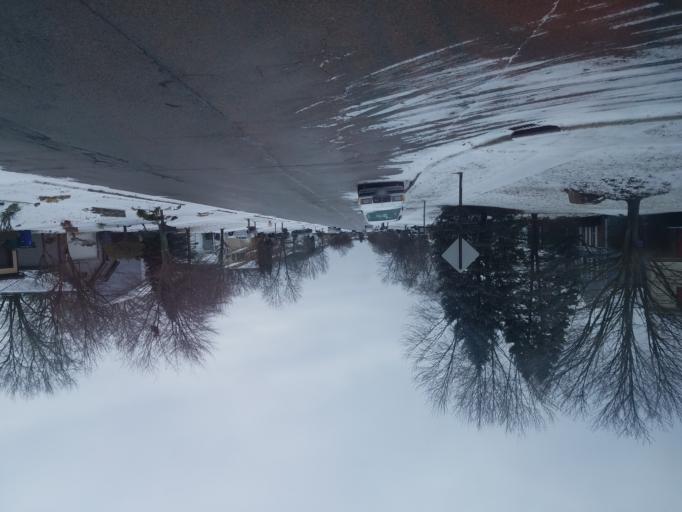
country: US
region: Ohio
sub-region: Delaware County
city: Powell
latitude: 40.1200
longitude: -83.0764
